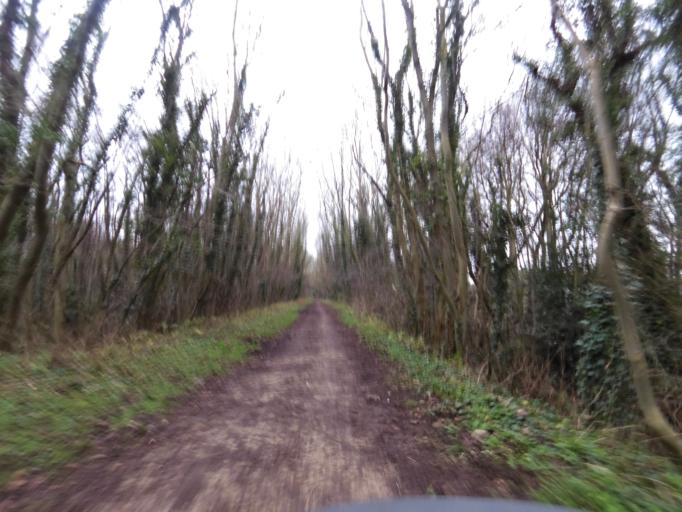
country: GB
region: England
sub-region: Norfolk
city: Mattishall
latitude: 52.7456
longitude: 1.0948
